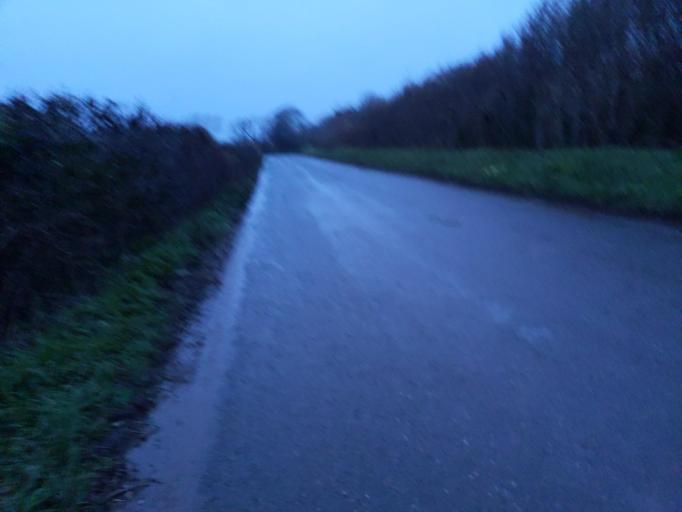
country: GB
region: England
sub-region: Devon
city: Yealmpton
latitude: 50.3355
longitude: -4.0147
